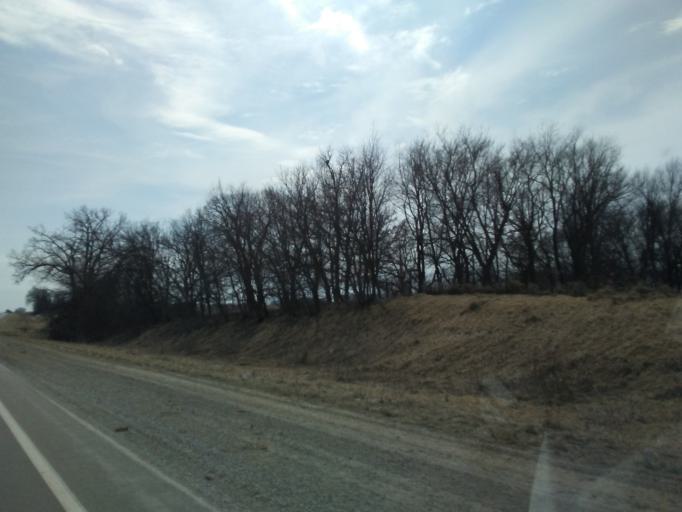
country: US
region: Iowa
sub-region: Winneshiek County
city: Decorah
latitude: 43.4279
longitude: -91.8594
